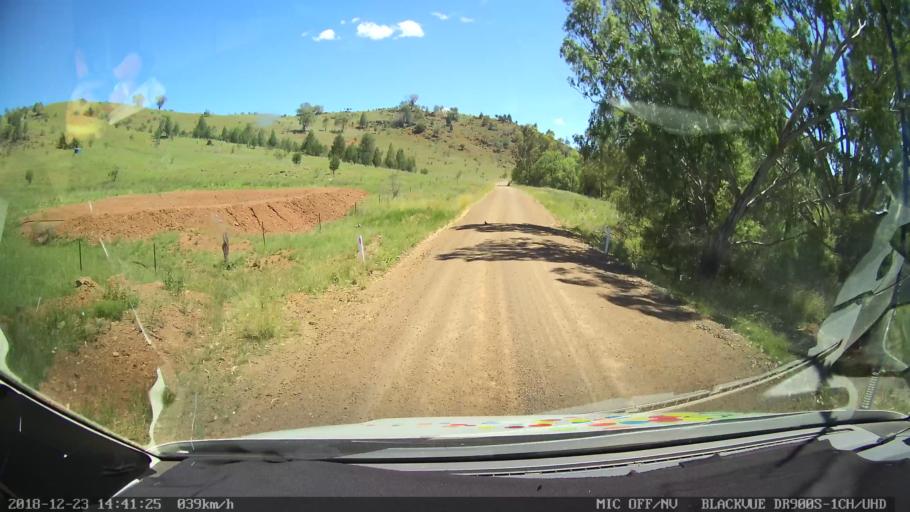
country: AU
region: New South Wales
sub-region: Tamworth Municipality
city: Manilla
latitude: -30.6313
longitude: 150.9021
